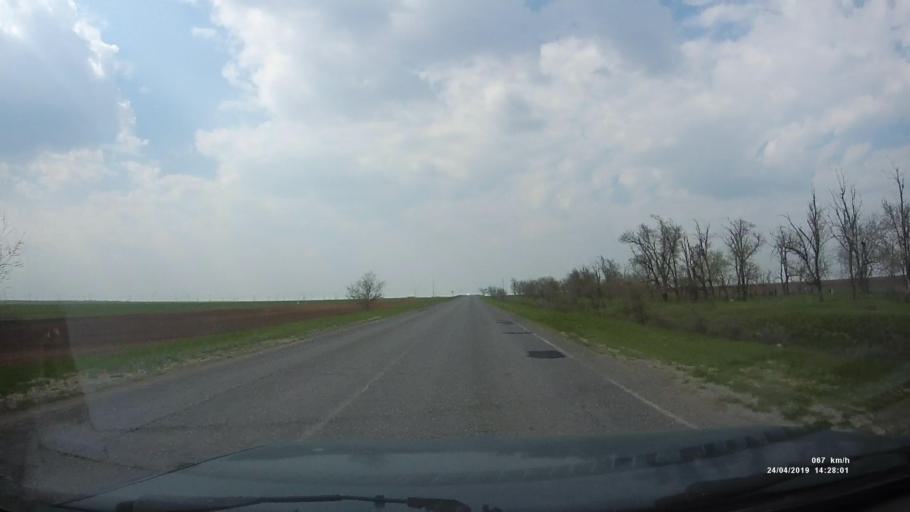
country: RU
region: Kalmykiya
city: Arshan'
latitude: 46.3356
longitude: 44.0340
